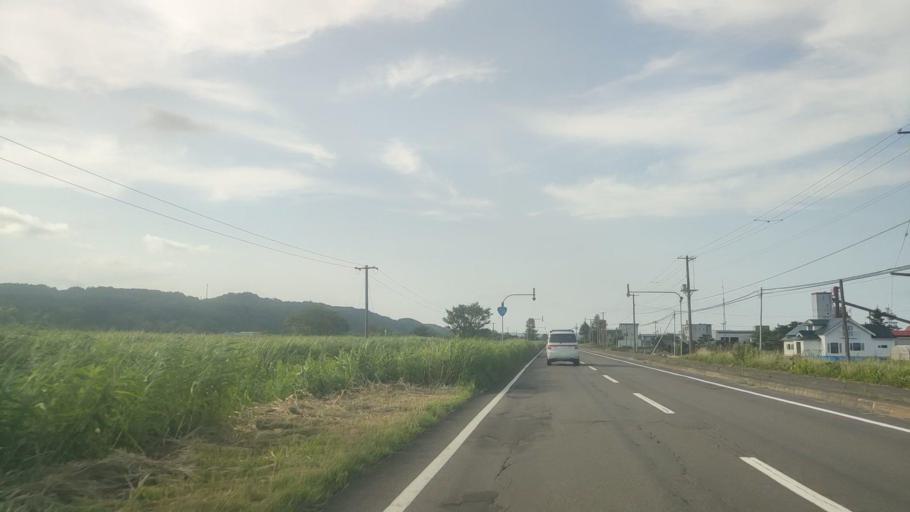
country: JP
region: Hokkaido
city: Iwamizawa
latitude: 42.9871
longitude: 141.7919
